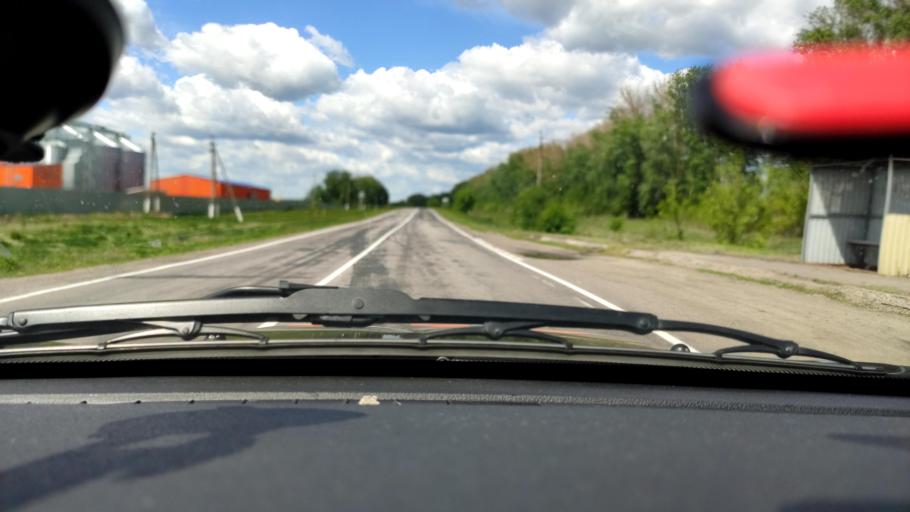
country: RU
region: Voronezj
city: Ostrogozhsk
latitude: 51.0554
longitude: 38.9098
